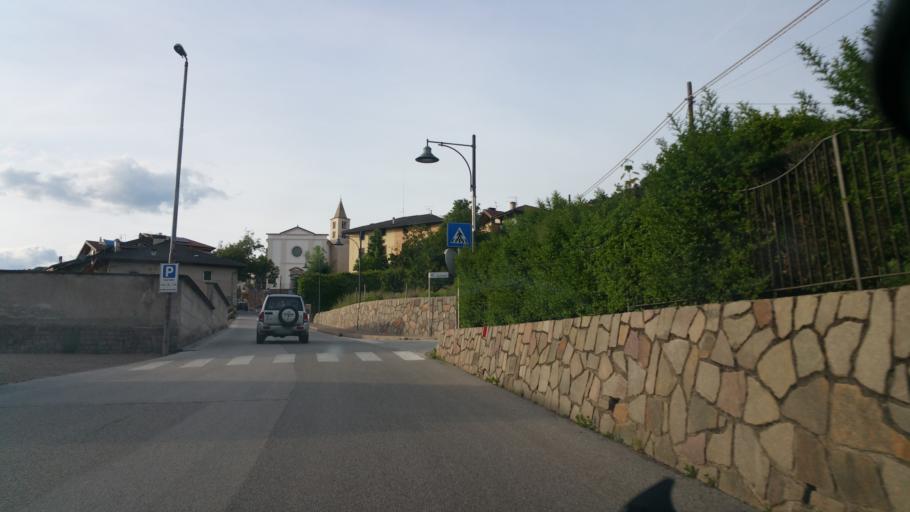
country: IT
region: Trentino-Alto Adige
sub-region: Provincia di Trento
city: Civezzano
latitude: 46.1050
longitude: 11.1841
